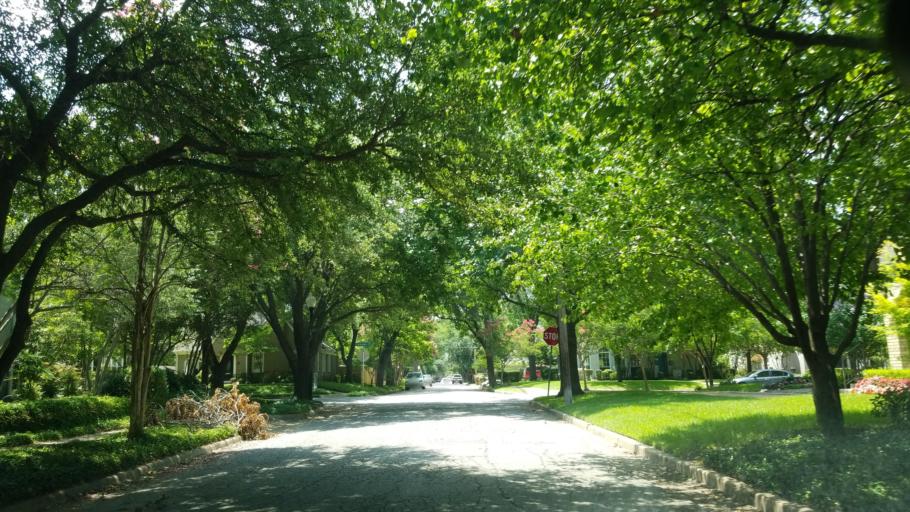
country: US
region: Texas
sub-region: Dallas County
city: Highland Park
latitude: 32.8259
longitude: -96.7774
